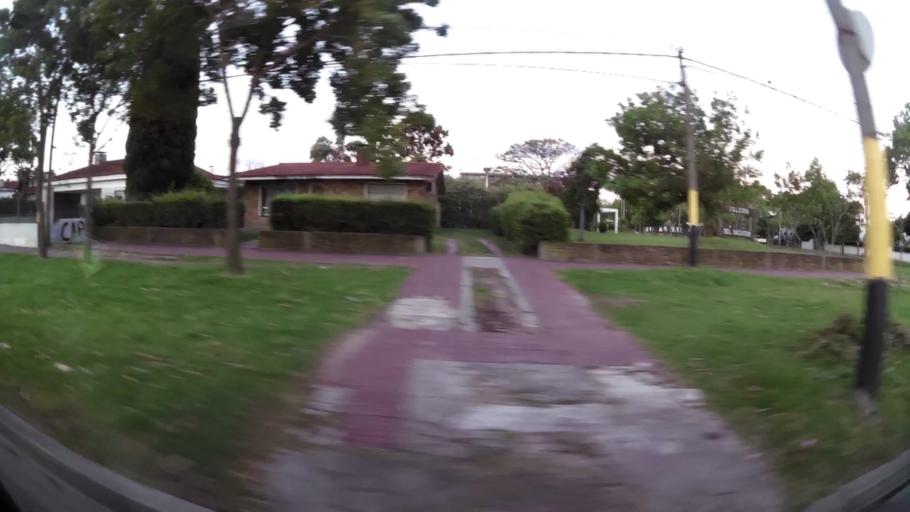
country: UY
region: Canelones
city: Paso de Carrasco
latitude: -34.8787
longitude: -56.0863
